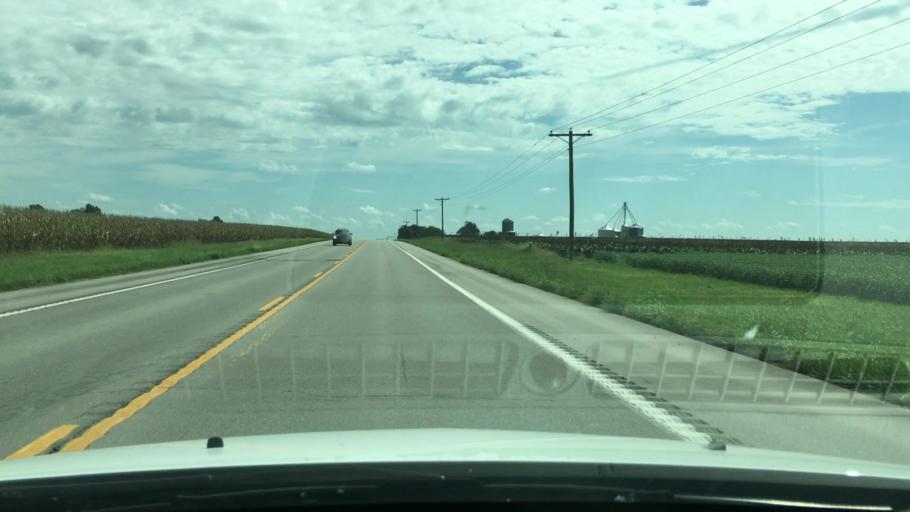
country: US
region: Missouri
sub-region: Audrain County
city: Mexico
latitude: 39.1638
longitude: -91.7478
